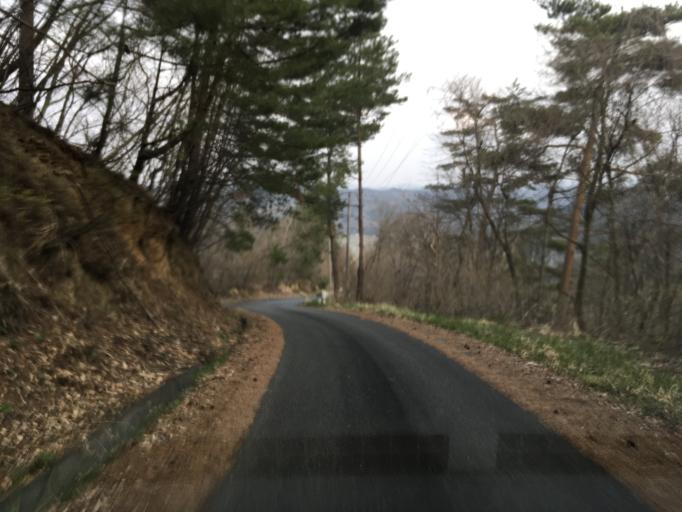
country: JP
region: Iwate
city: Ichinoseki
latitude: 38.9412
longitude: 141.2366
